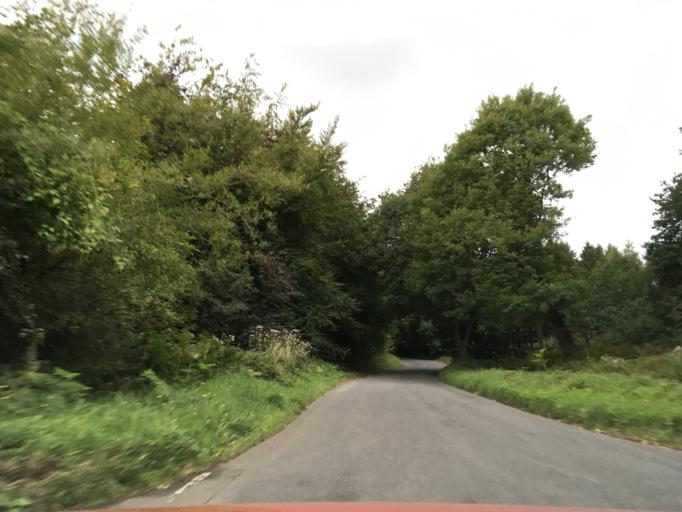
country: GB
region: Wales
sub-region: Newport
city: Llanvaches
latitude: 51.6428
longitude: -2.8283
